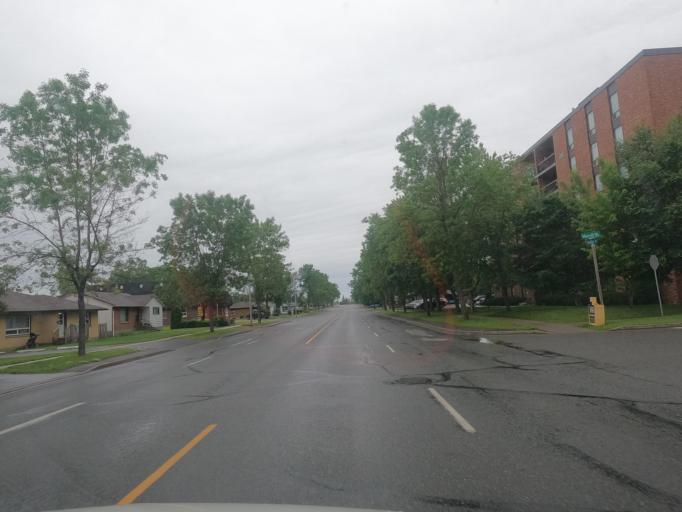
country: CA
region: Ontario
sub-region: Thunder Bay District
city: Thunder Bay
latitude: 48.4617
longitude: -89.1824
